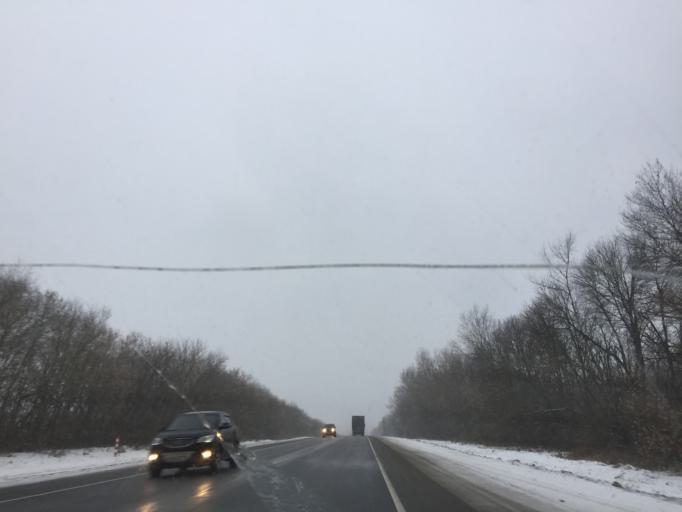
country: RU
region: Tula
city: Plavsk
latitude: 53.7624
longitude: 37.3398
